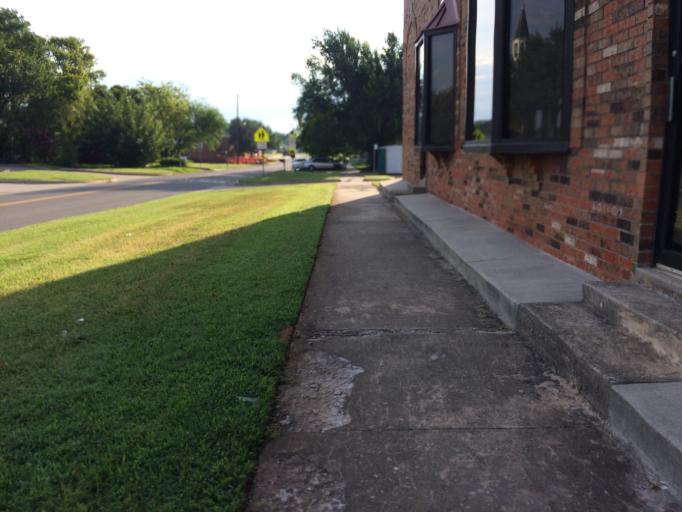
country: US
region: Oklahoma
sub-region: Cleveland County
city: Norman
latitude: 35.2237
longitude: -97.4394
